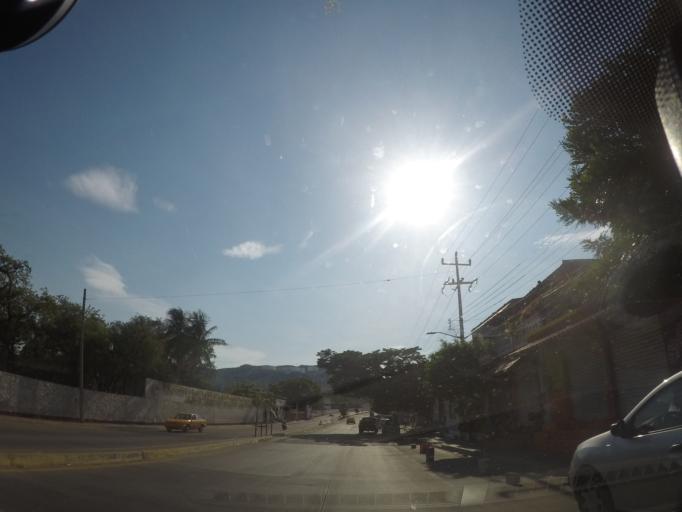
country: MX
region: Oaxaca
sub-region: Salina Cruz
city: Salina Cruz
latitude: 16.1725
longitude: -95.2000
